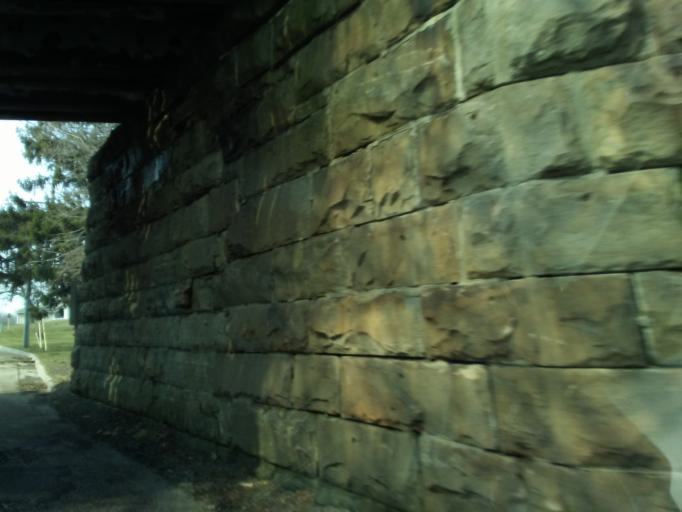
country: US
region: Wisconsin
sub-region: Columbia County
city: Lodi
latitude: 43.3087
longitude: -89.5292
